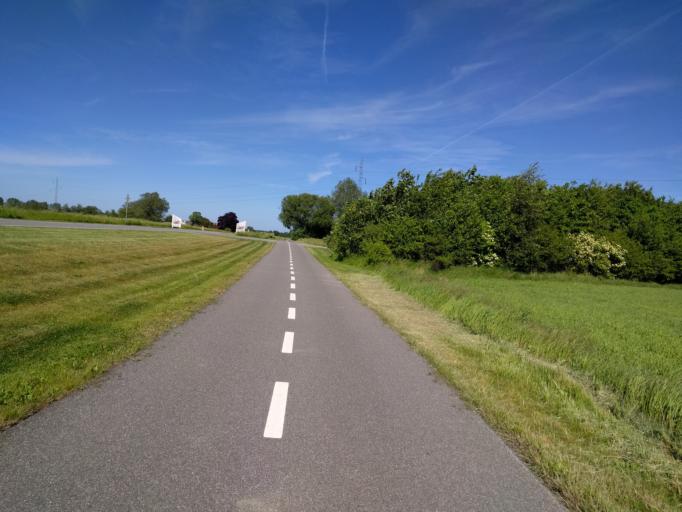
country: DK
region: South Denmark
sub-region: Kerteminde Kommune
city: Kerteminde
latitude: 55.4132
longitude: 10.6326
